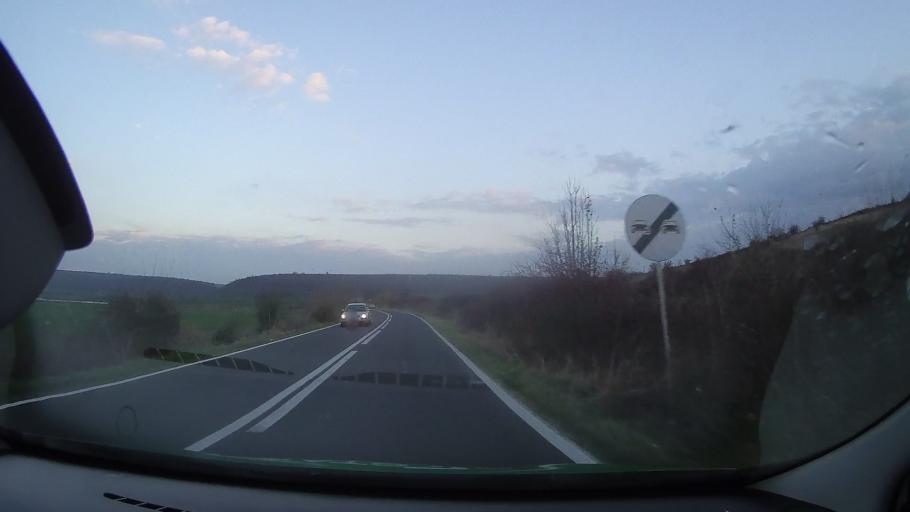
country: RO
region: Constanta
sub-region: Comuna Lipnita
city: Lipnita
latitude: 44.0969
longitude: 27.6332
